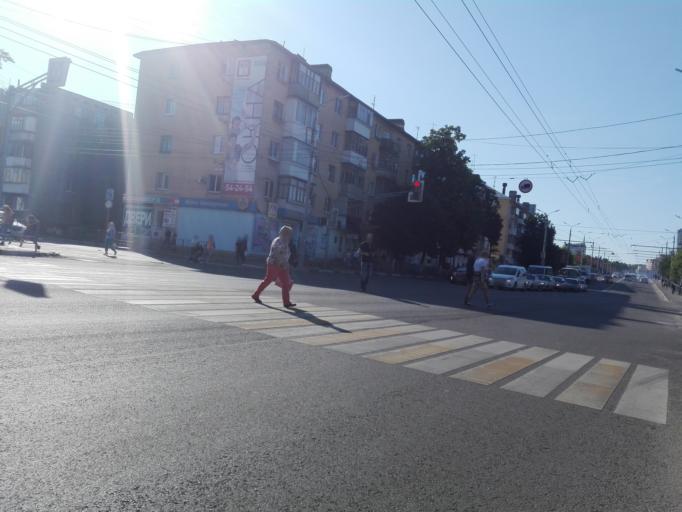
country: RU
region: Orjol
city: Orel
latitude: 52.9730
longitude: 36.0839
